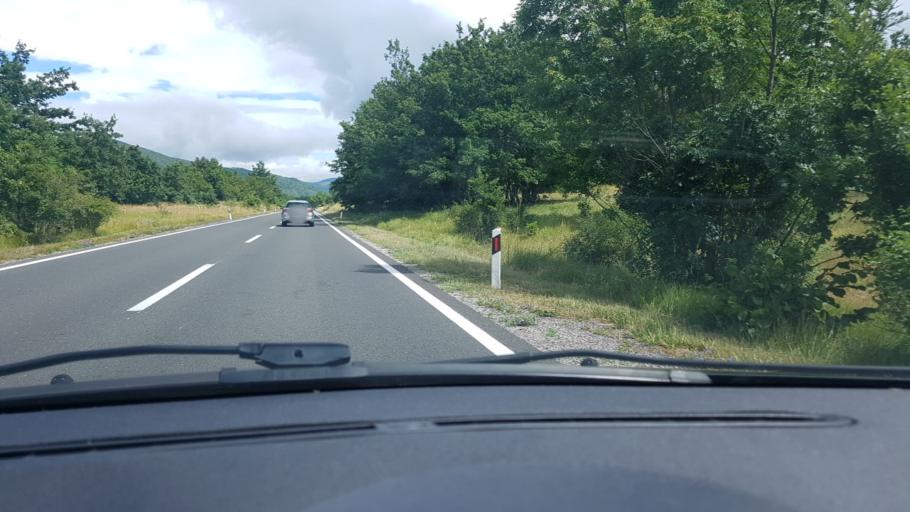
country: HR
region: Zadarska
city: Gracac
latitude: 44.4565
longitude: 15.8217
